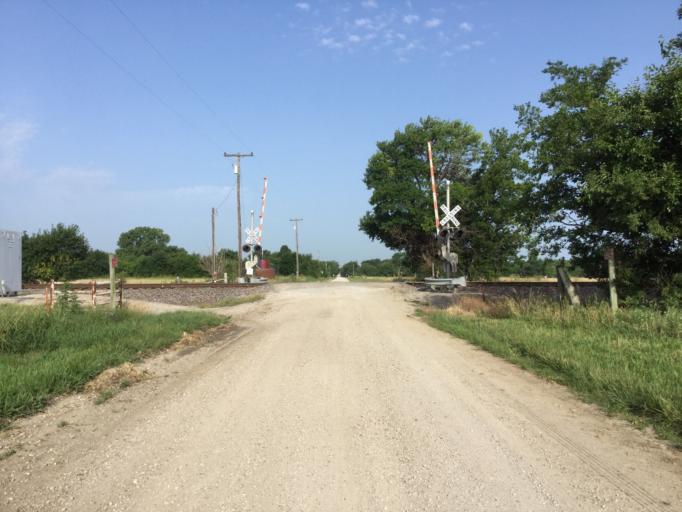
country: US
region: Kansas
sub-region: Montgomery County
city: Independence
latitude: 37.1386
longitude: -95.7603
